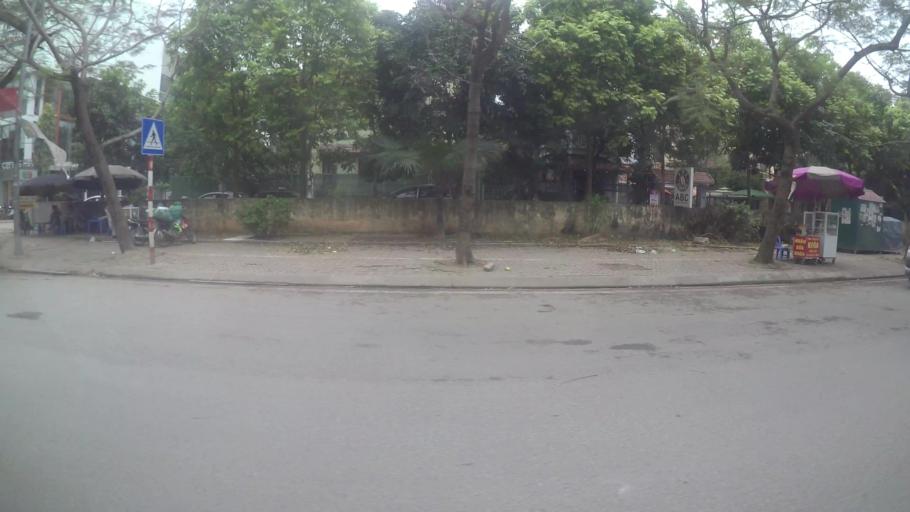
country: VN
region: Ha Noi
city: Tay Ho
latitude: 21.0682
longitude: 105.8032
